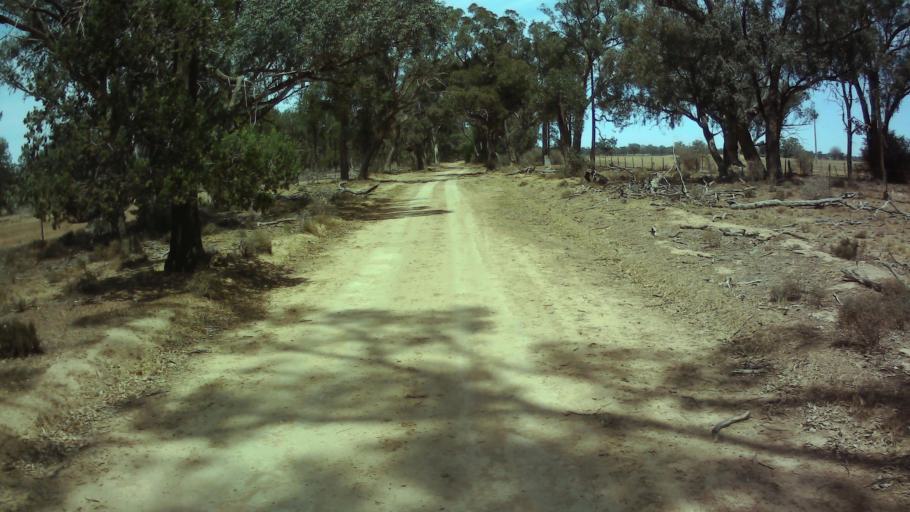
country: AU
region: New South Wales
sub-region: Weddin
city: Grenfell
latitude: -34.0300
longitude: 147.9363
